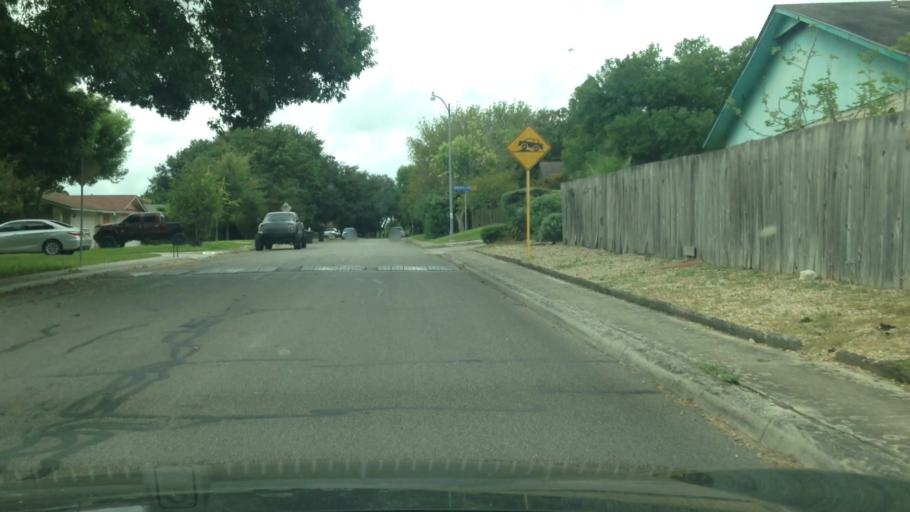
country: US
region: Texas
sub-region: Bexar County
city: Windcrest
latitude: 29.5745
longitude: -98.4114
